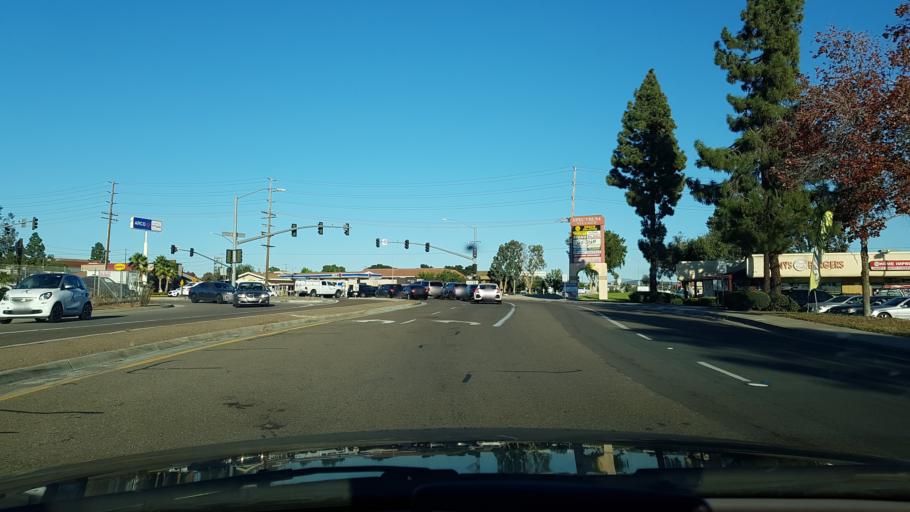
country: US
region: California
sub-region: San Diego County
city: San Diego
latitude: 32.8311
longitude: -117.1392
